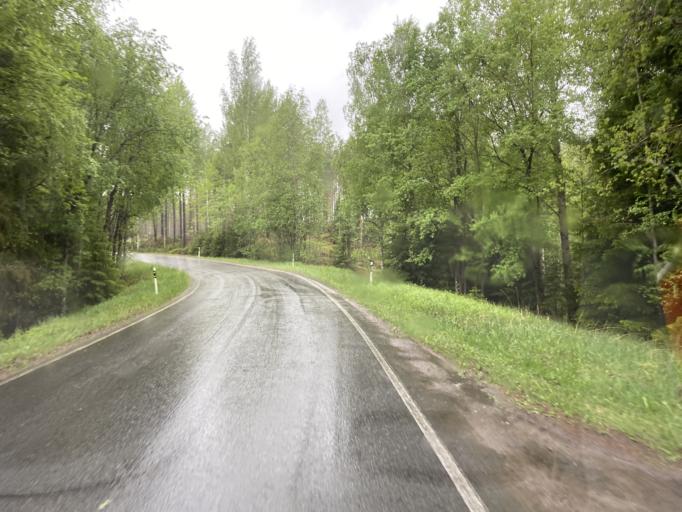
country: FI
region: Haeme
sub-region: Forssa
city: Humppila
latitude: 61.0898
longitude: 23.3096
